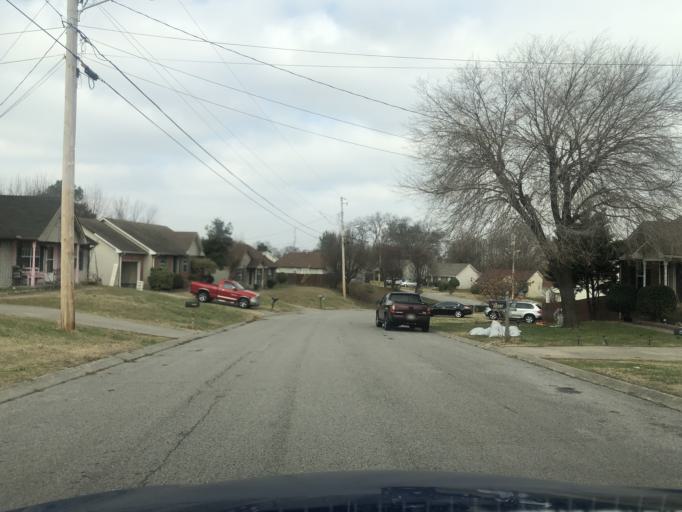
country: US
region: Tennessee
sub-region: Davidson County
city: Oak Hill
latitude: 36.0902
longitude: -86.7074
